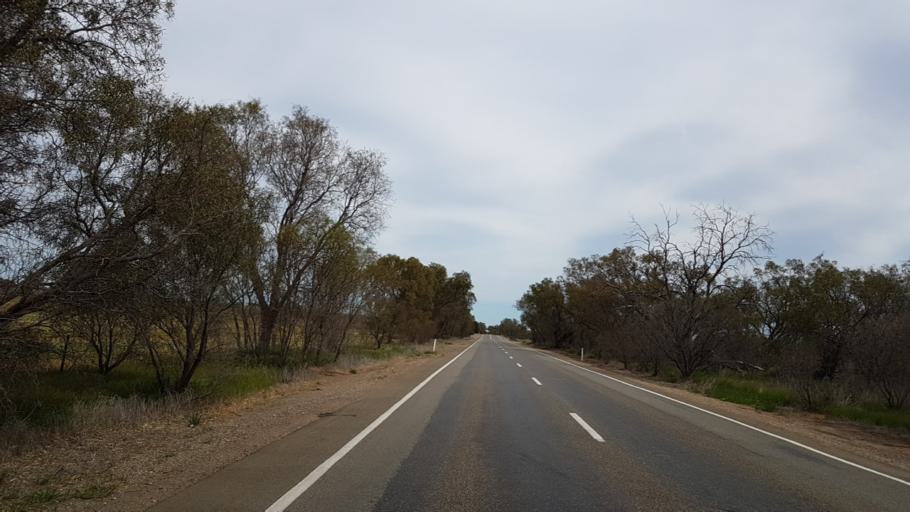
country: AU
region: South Australia
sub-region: Northern Areas
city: Jamestown
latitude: -33.2204
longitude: 138.4119
